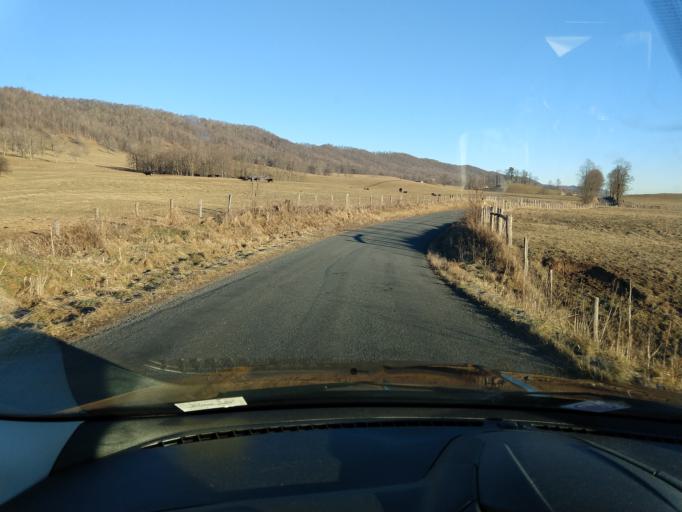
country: US
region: Virginia
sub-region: Highland County
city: Monterey
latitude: 38.3851
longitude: -79.6628
